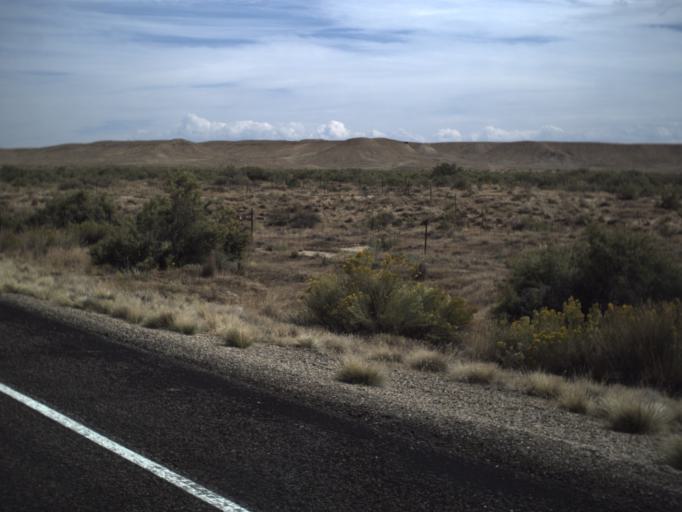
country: US
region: Utah
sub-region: Grand County
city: Moab
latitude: 38.9553
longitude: -109.7502
